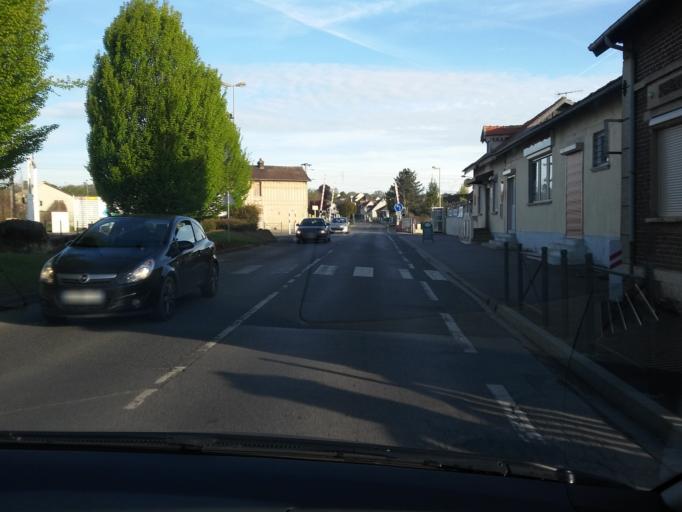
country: FR
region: Picardie
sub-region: Departement de l'Oise
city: Le Meux
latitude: 49.3589
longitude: 2.7542
